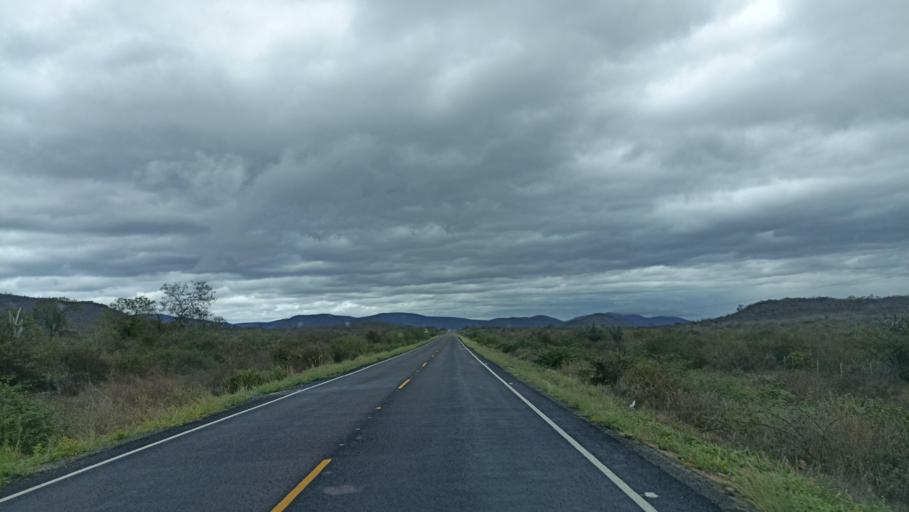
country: BR
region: Bahia
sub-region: Iacu
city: Iacu
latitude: -12.9033
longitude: -40.4040
